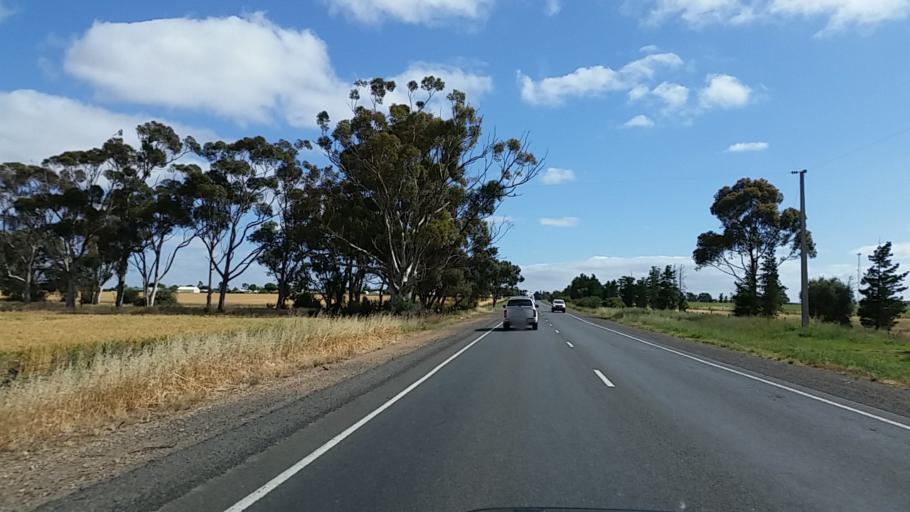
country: AU
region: South Australia
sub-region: Light
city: Roseworthy
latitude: -34.5438
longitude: 138.7493
